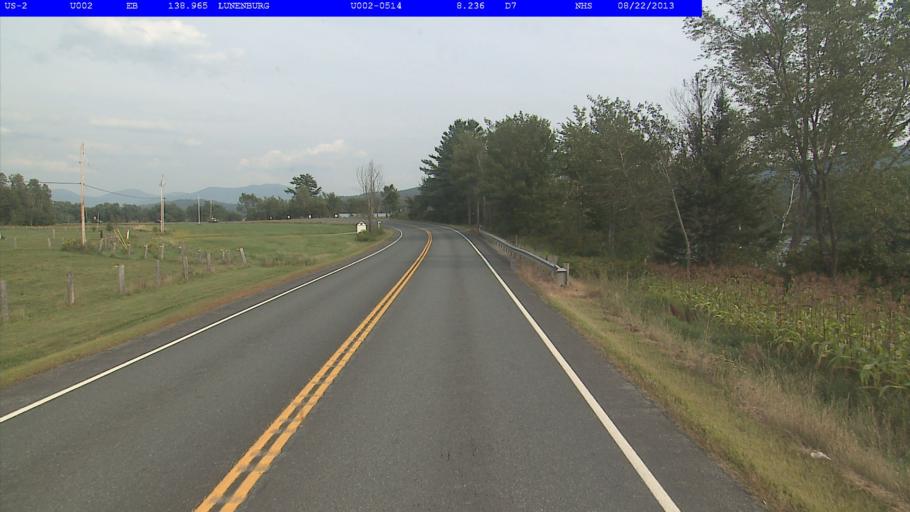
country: US
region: New Hampshire
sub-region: Coos County
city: Lancaster
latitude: 44.4843
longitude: -71.6262
